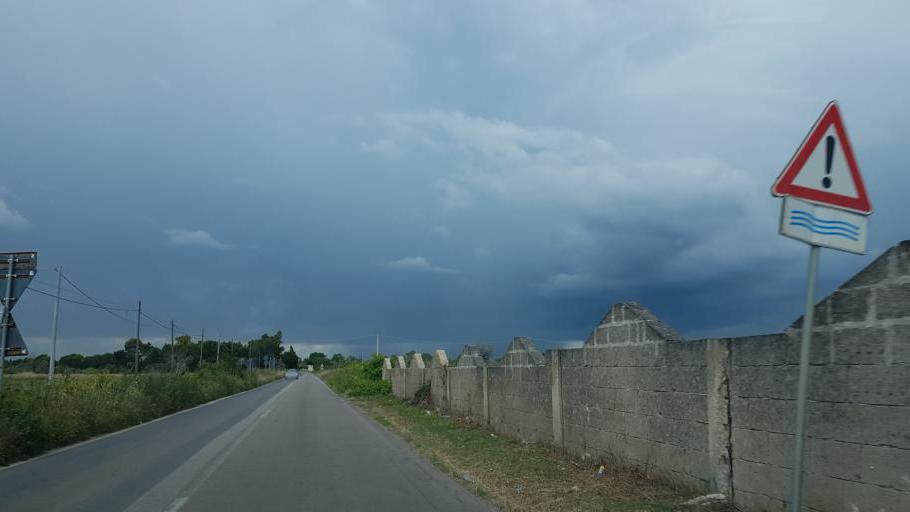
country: IT
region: Apulia
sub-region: Provincia di Lecce
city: Porto Cesareo
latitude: 40.3039
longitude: 17.8606
